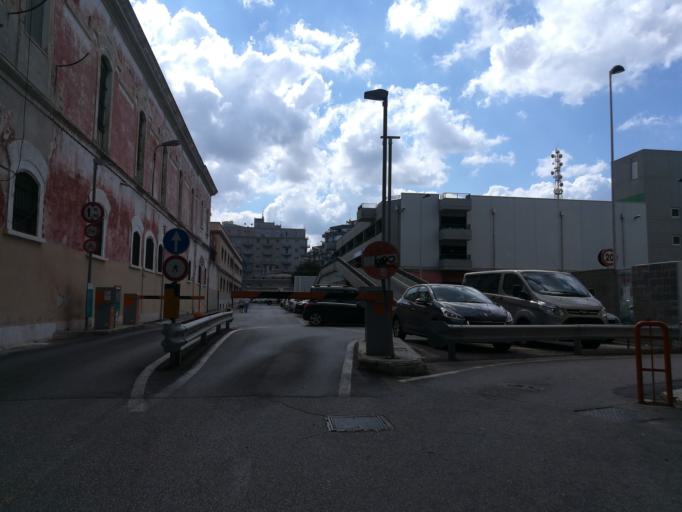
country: IT
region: Apulia
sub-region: Provincia di Bari
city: Bari
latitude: 41.1192
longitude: 16.8760
